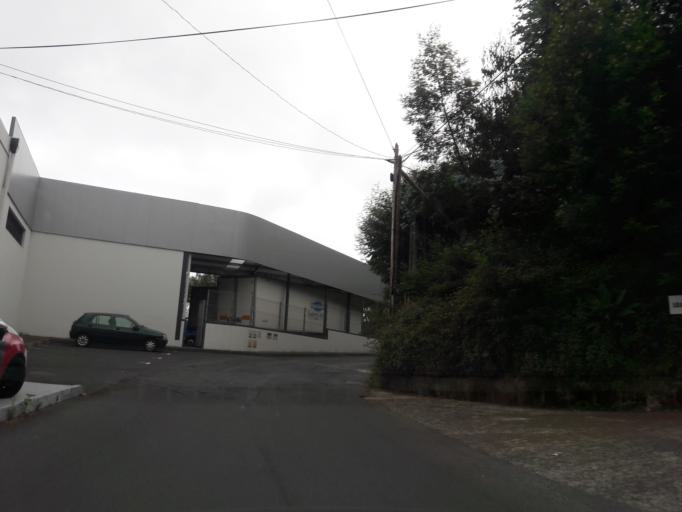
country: PT
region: Madeira
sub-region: Santa Cruz
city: Camacha
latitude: 32.6593
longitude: -16.8583
